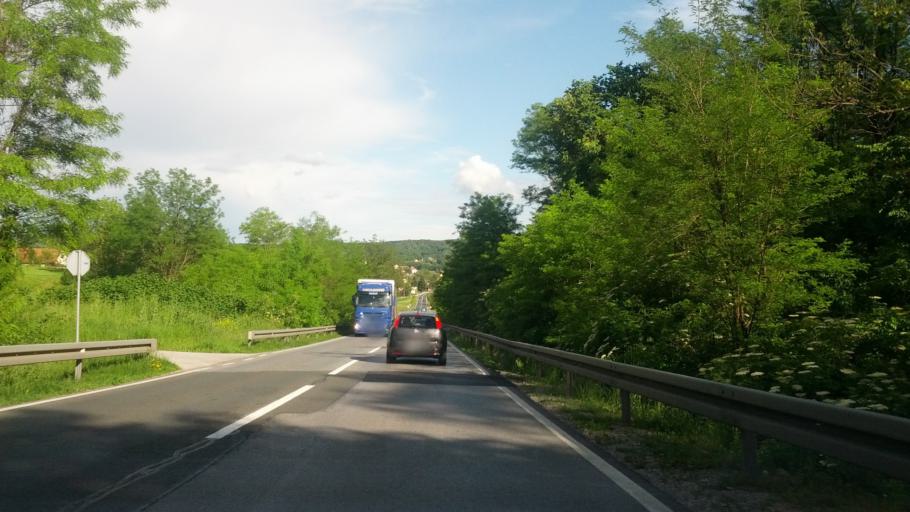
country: HR
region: Karlovacka
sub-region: Grad Karlovac
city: Karlovac
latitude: 45.4358
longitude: 15.5920
